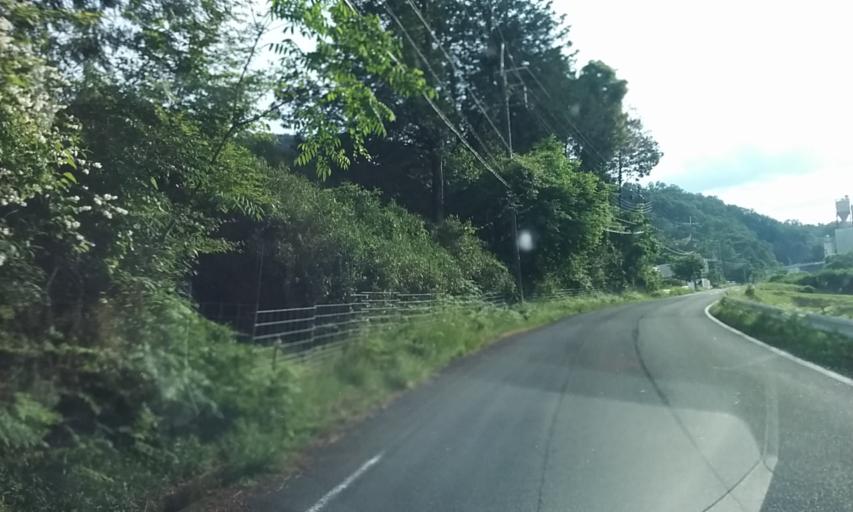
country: JP
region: Kyoto
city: Ayabe
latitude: 35.2018
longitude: 135.3822
